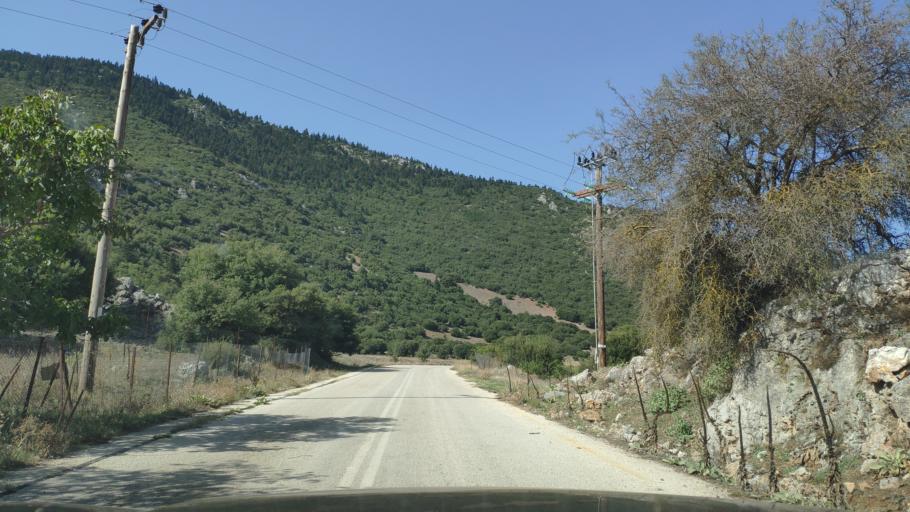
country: GR
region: West Greece
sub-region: Nomos Achaias
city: Aiyira
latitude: 37.9604
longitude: 22.3458
